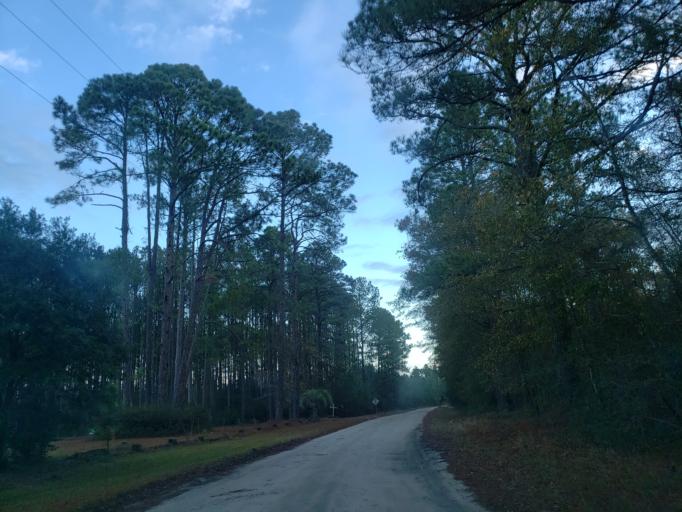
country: US
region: Georgia
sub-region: Chatham County
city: Bloomingdale
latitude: 32.1156
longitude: -81.3438
